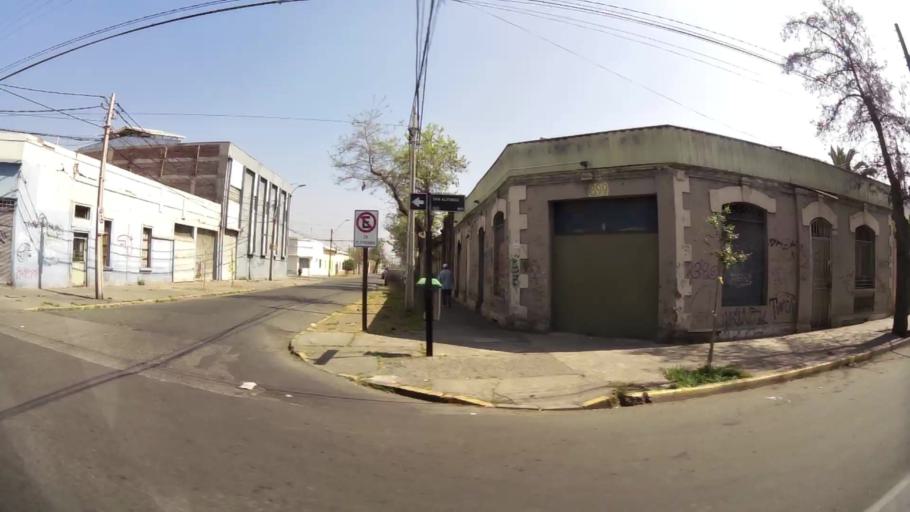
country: CL
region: Santiago Metropolitan
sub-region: Provincia de Santiago
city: Santiago
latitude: -33.4606
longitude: -70.6744
